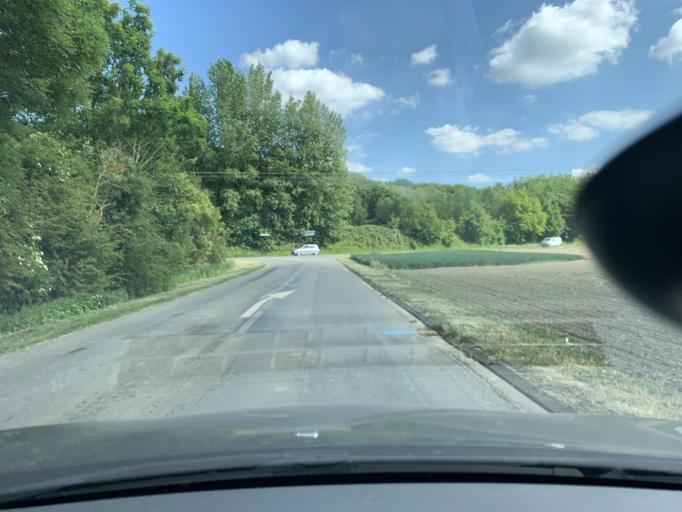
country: FR
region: Nord-Pas-de-Calais
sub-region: Departement du Pas-de-Calais
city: Oisy-le-Verger
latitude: 50.2360
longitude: 3.1074
